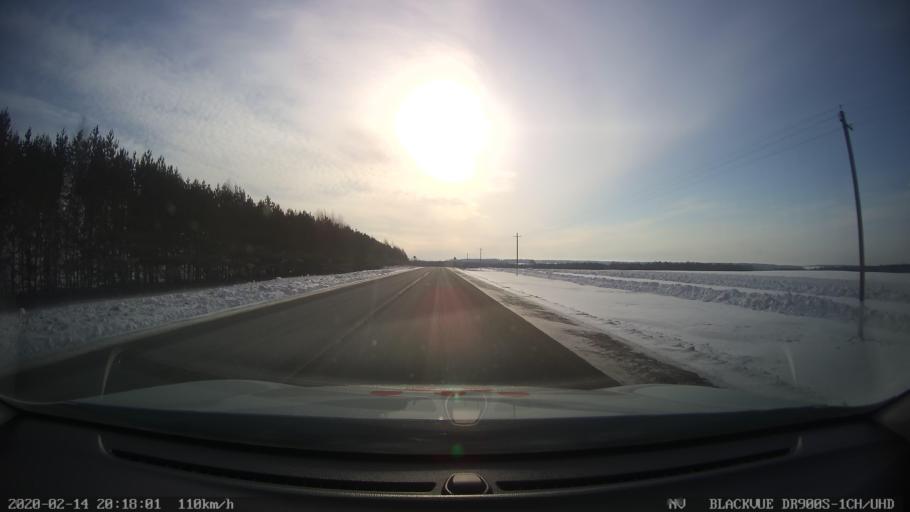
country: RU
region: Tatarstan
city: Verkhniy Uslon
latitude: 55.5920
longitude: 48.8834
